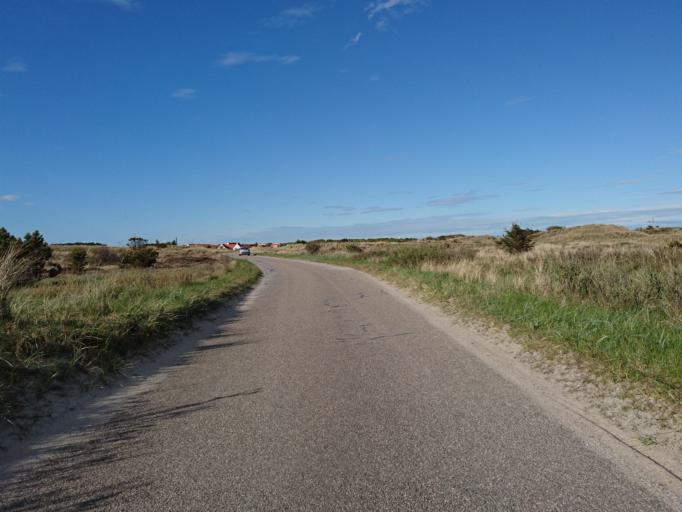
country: DK
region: North Denmark
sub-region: Frederikshavn Kommune
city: Skagen
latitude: 57.7107
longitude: 10.5633
